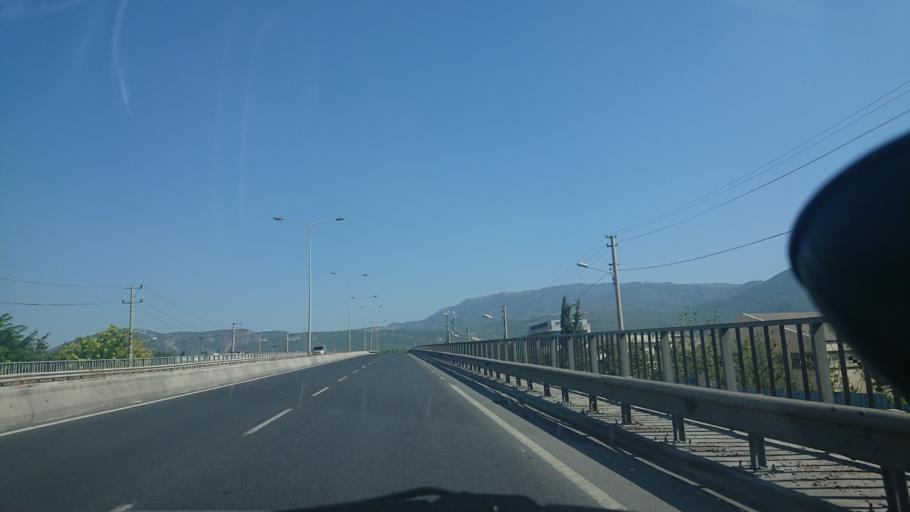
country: TR
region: Izmir
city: Bornova
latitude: 38.4532
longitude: 27.2635
